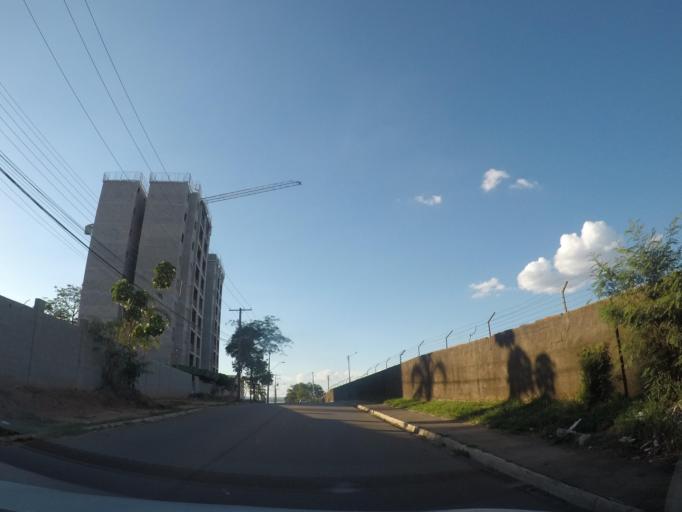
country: BR
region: Sao Paulo
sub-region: Sumare
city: Sumare
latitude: -22.8090
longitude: -47.2476
